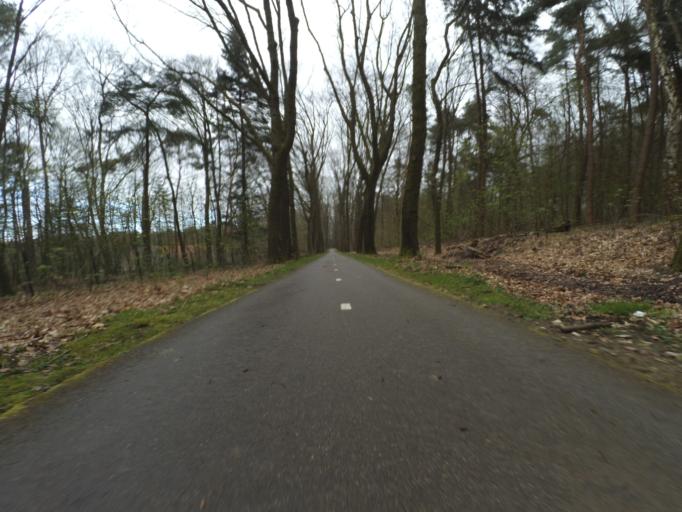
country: NL
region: Gelderland
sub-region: Gemeente Arnhem
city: Burgemeesterswijk
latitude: 52.0119
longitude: 5.9168
